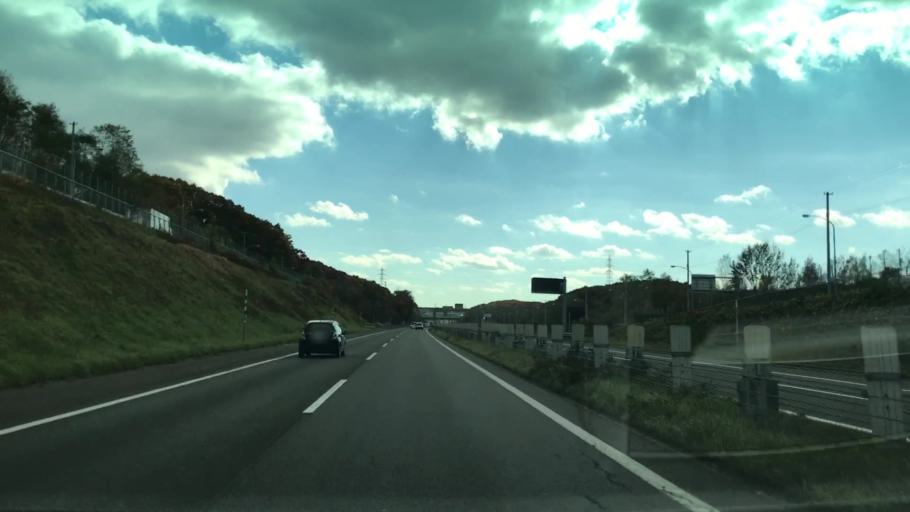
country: JP
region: Hokkaido
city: Kitahiroshima
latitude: 43.0084
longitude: 141.4664
